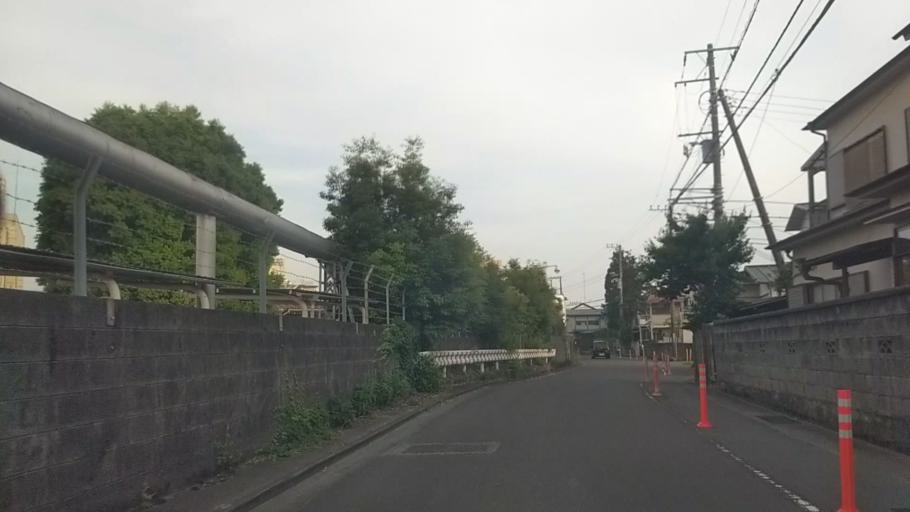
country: JP
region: Kanagawa
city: Odawara
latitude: 35.2667
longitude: 139.1618
